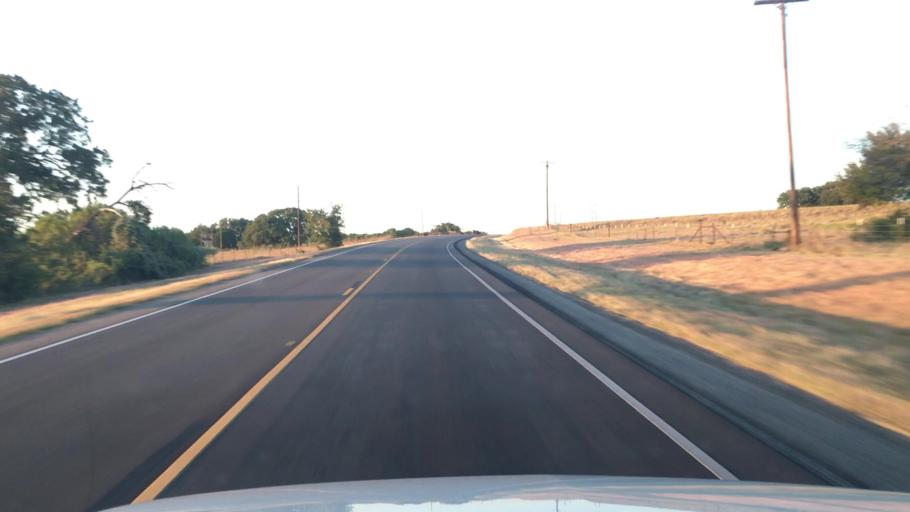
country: US
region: Texas
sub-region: Hamilton County
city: Hico
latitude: 32.0587
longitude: -97.9967
